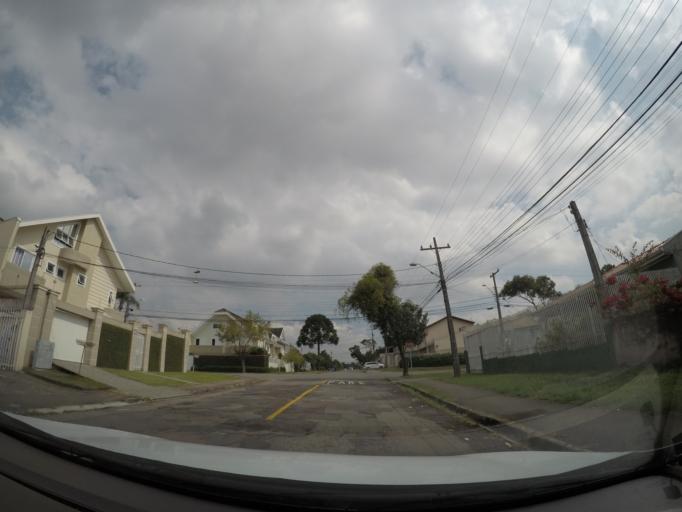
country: BR
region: Parana
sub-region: Sao Jose Dos Pinhais
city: Sao Jose dos Pinhais
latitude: -25.5034
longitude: -49.2431
